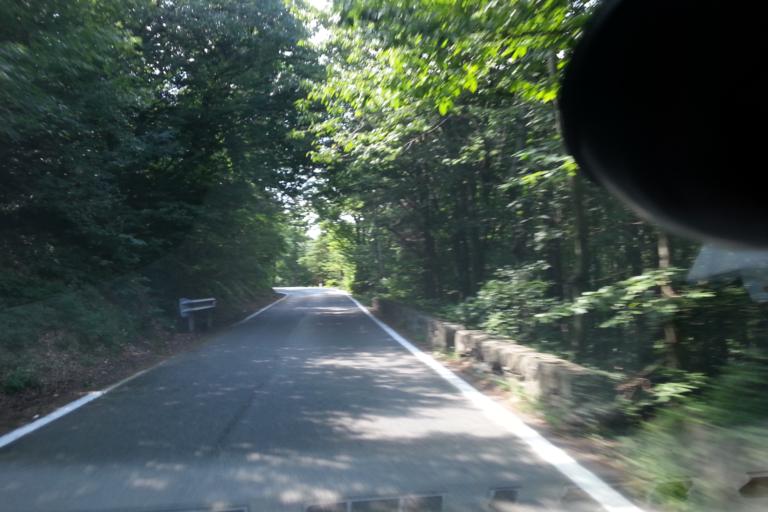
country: IT
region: Piedmont
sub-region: Provincia di Torino
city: Chiusa di San Michele
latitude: 45.0934
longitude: 7.3442
